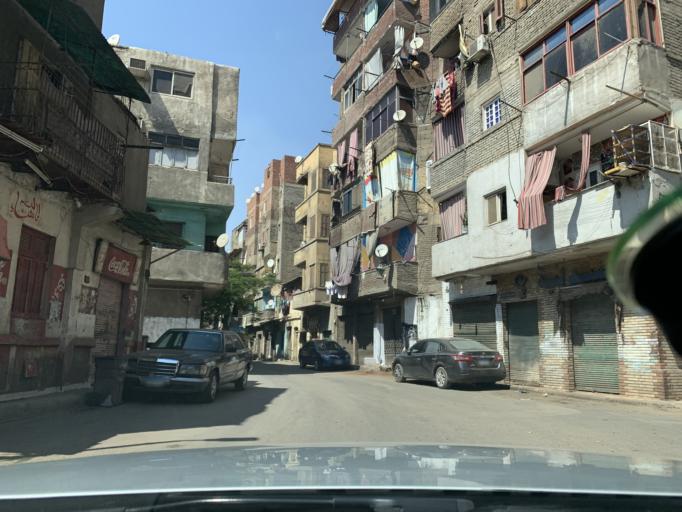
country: EG
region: Muhafazat al Qahirah
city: Cairo
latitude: 30.0704
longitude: 31.2556
